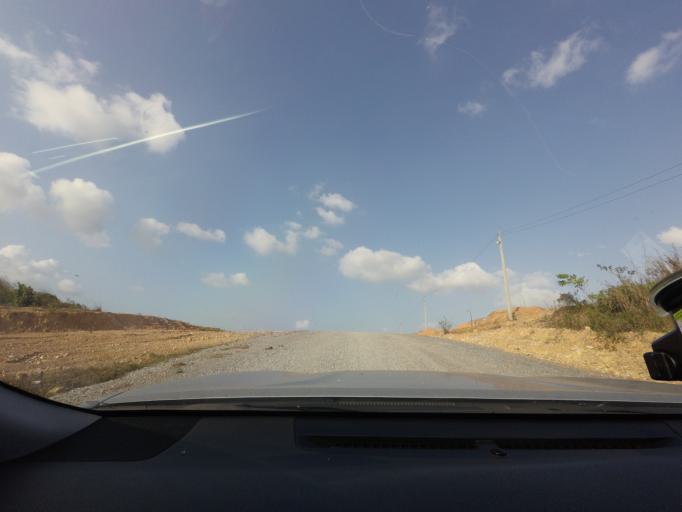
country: TH
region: Pattani
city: Mae Lan
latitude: 6.6116
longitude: 101.2557
